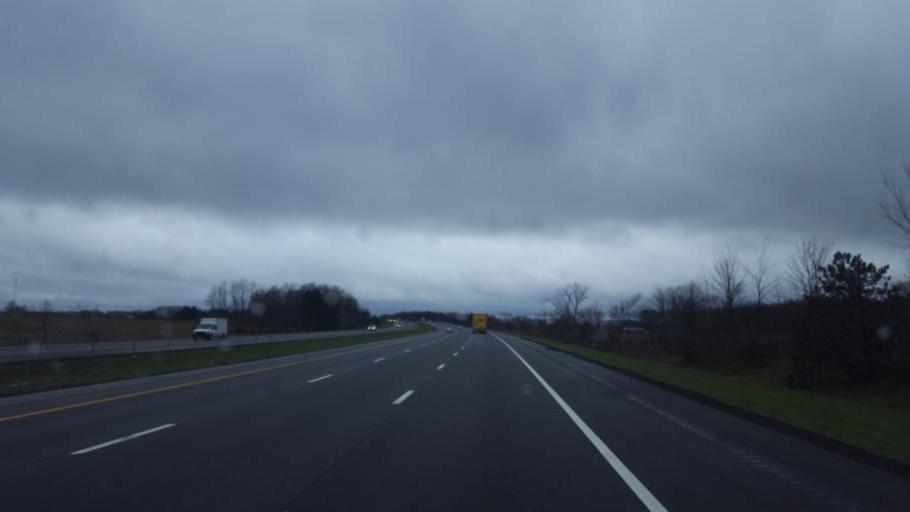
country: US
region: Ohio
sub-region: Morrow County
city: Cardington
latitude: 40.4368
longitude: -82.8097
